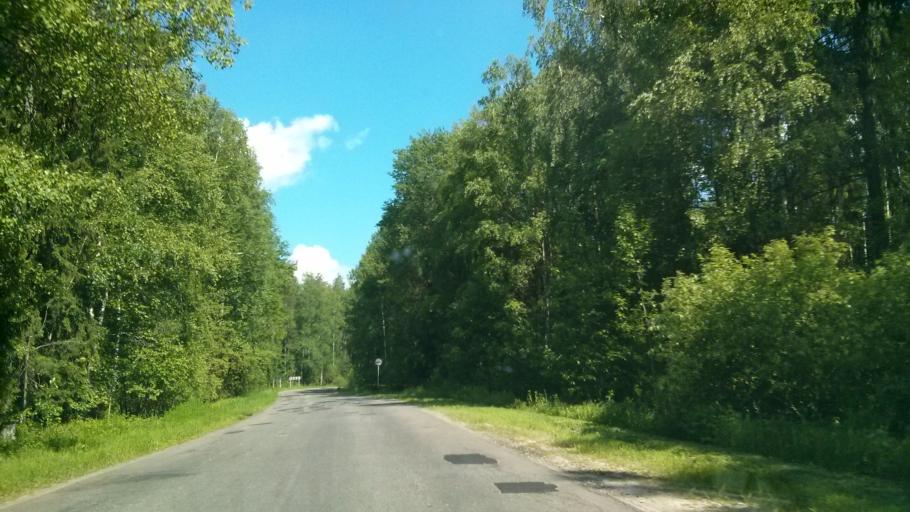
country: RU
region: Vladimir
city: Melenki
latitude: 55.3318
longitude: 41.6930
